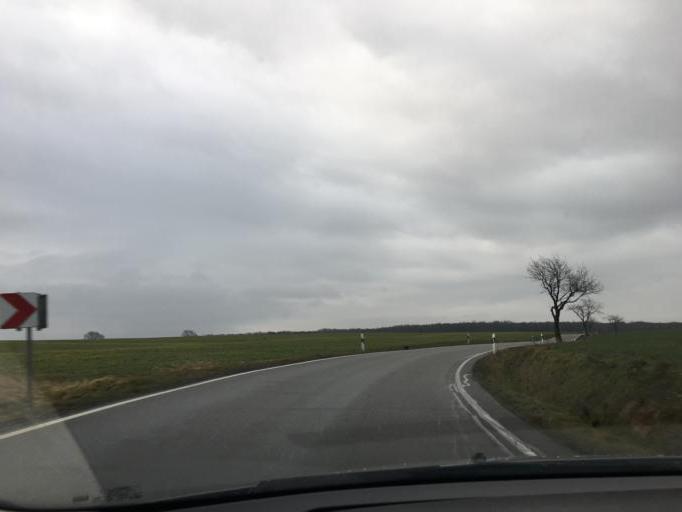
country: DE
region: Saxony
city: Pfaffroda
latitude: 50.8717
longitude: 12.5401
